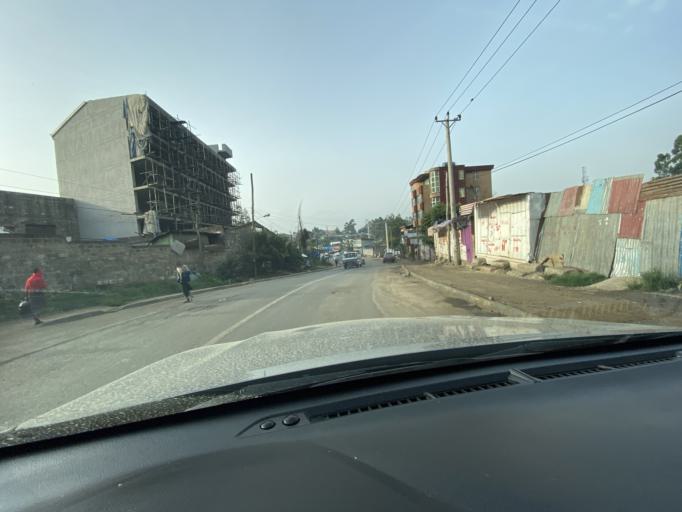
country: ET
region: Adis Abeba
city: Addis Ababa
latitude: 9.0212
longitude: 38.7223
